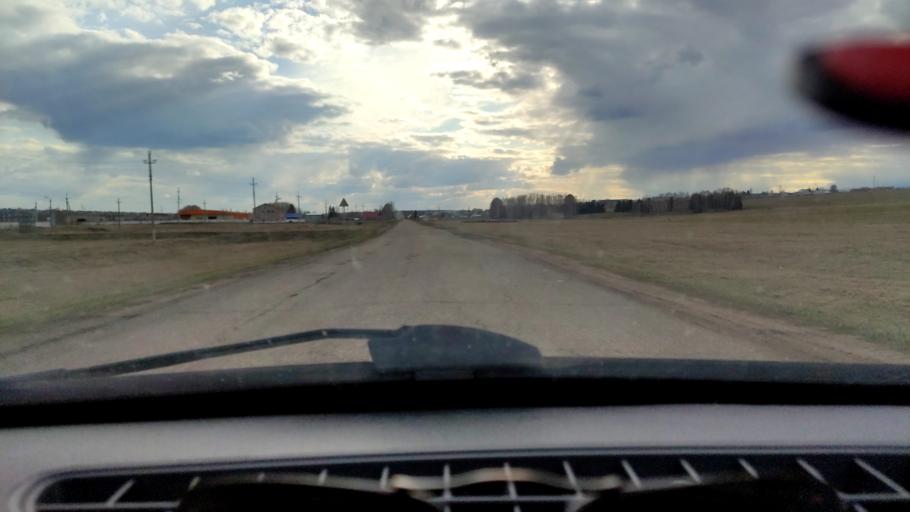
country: RU
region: Bashkortostan
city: Karmaskaly
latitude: 54.3810
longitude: 56.2177
